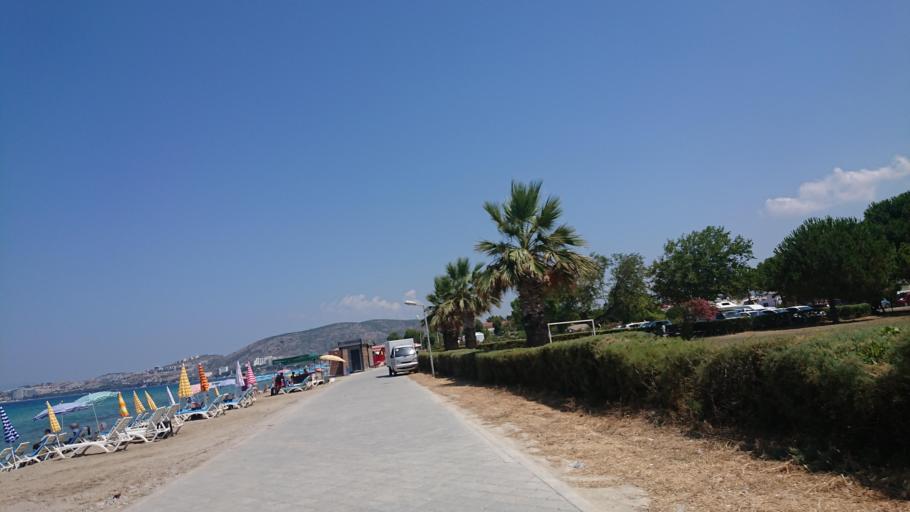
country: TR
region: Aydin
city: Kusadasi
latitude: 37.7969
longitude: 27.2684
